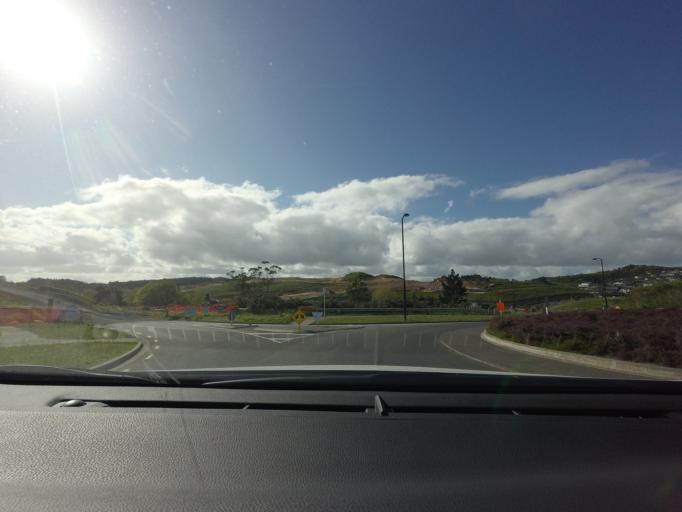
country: NZ
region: Auckland
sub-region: Auckland
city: Rothesay Bay
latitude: -36.5931
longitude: 174.6708
